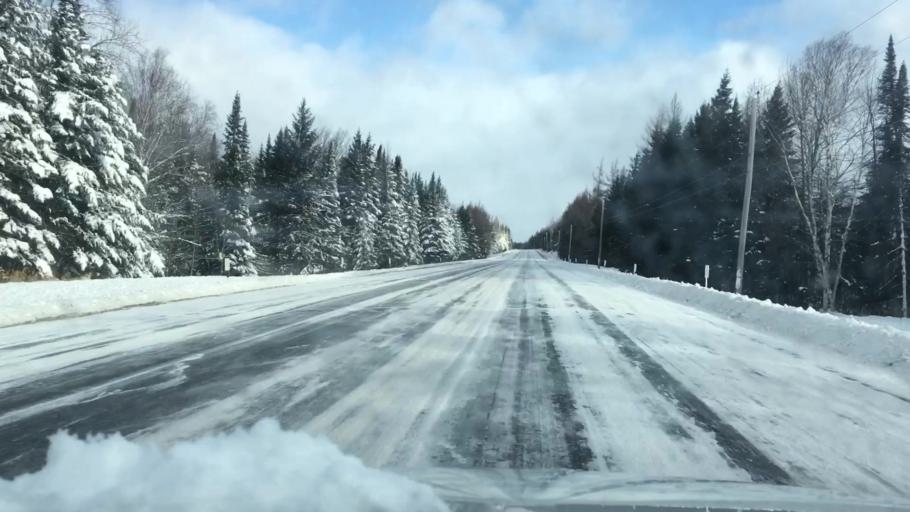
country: US
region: Maine
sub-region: Aroostook County
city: Van Buren
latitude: 47.0596
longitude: -67.9917
